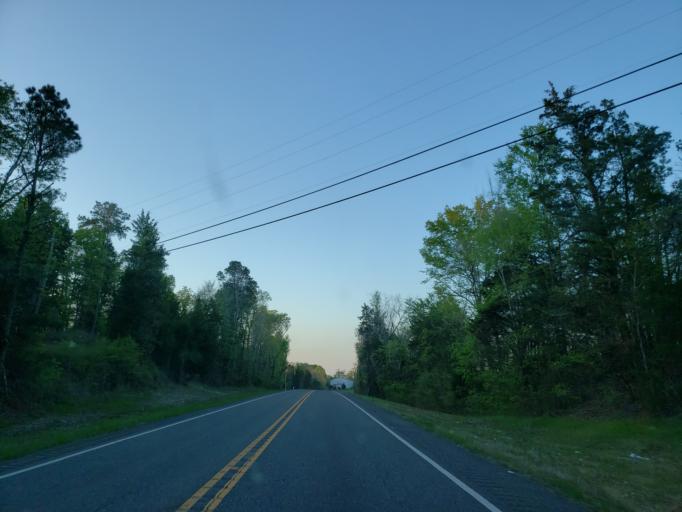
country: US
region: Alabama
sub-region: Sumter County
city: Livingston
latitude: 32.6433
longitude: -88.1715
